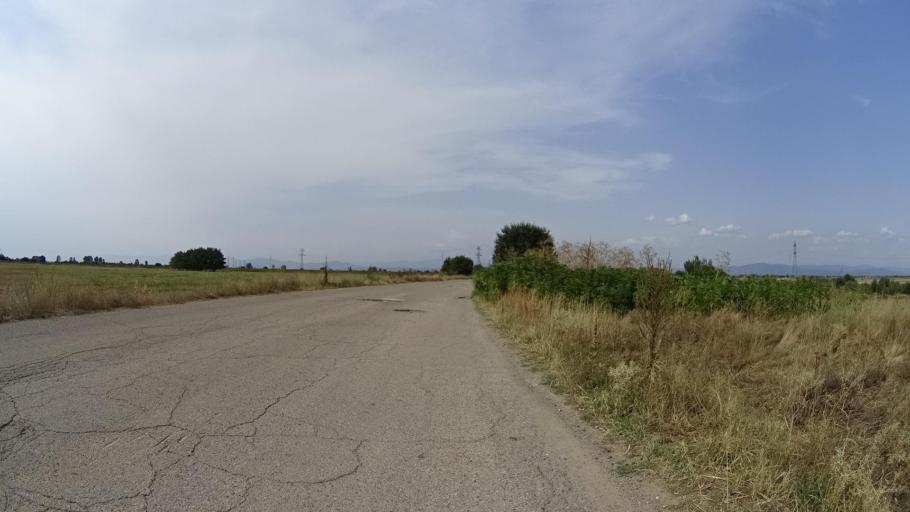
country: BG
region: Plovdiv
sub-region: Obshtina Kaloyanovo
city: Kaloyanovo
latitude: 42.3179
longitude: 24.7992
